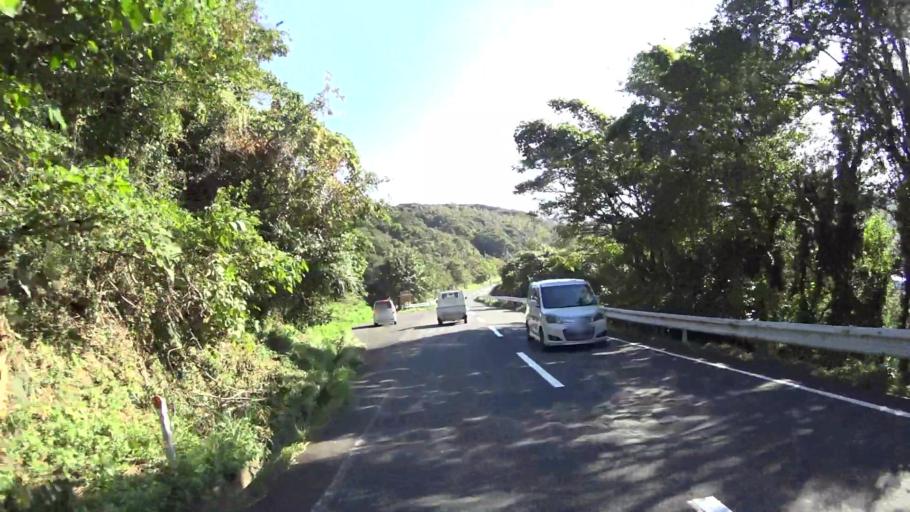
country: JP
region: Kyoto
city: Miyazu
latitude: 35.7123
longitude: 135.0691
